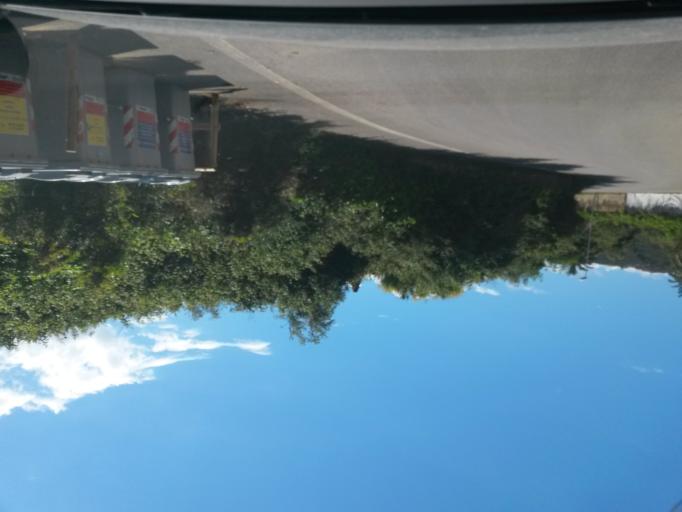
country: IT
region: Tuscany
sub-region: Provincia di Livorno
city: Rio Marina
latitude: 42.8623
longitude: 10.4182
